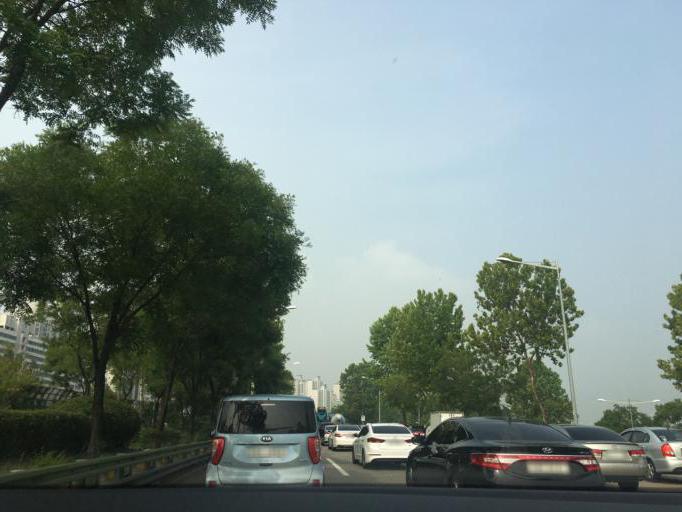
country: KR
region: Gyeonggi-do
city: Seongnam-si
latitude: 37.5189
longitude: 127.0938
